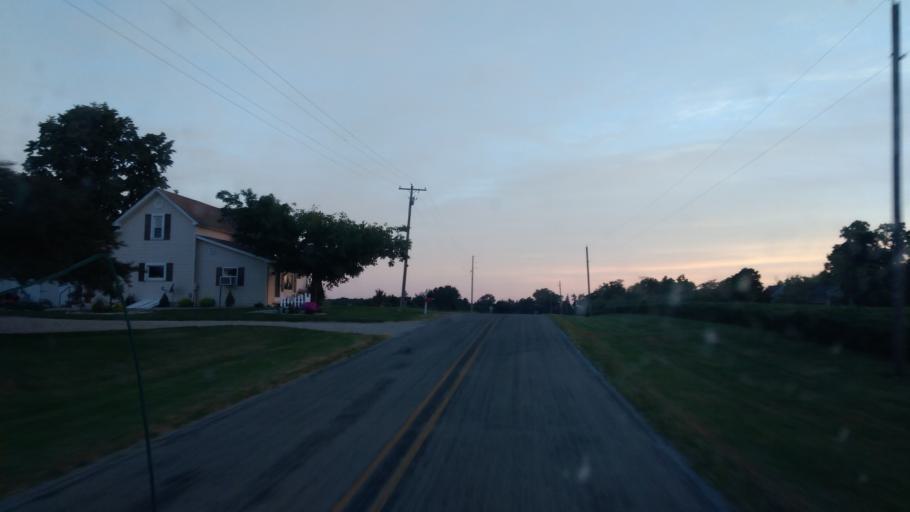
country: US
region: Indiana
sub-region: Wells County
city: Bluffton
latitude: 40.6831
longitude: -85.1362
